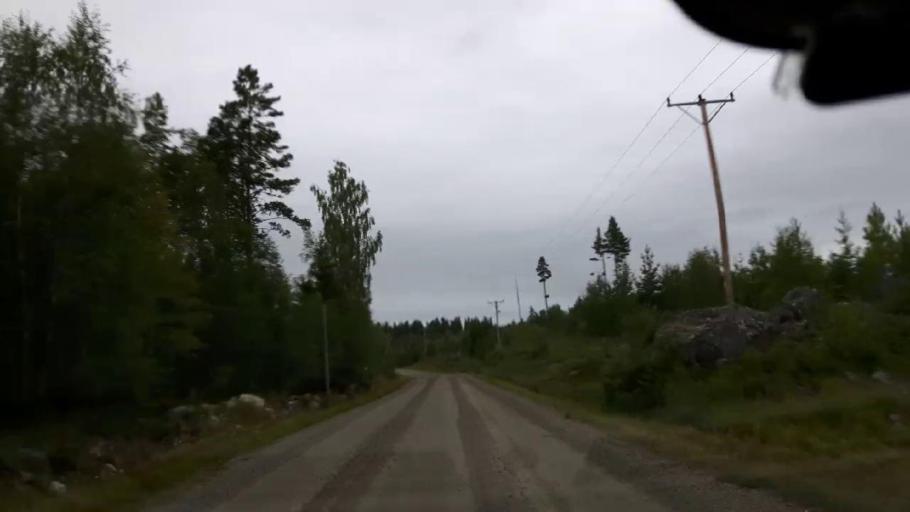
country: SE
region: Vaesternorrland
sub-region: Ange Kommun
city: Fransta
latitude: 62.7918
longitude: 16.0395
